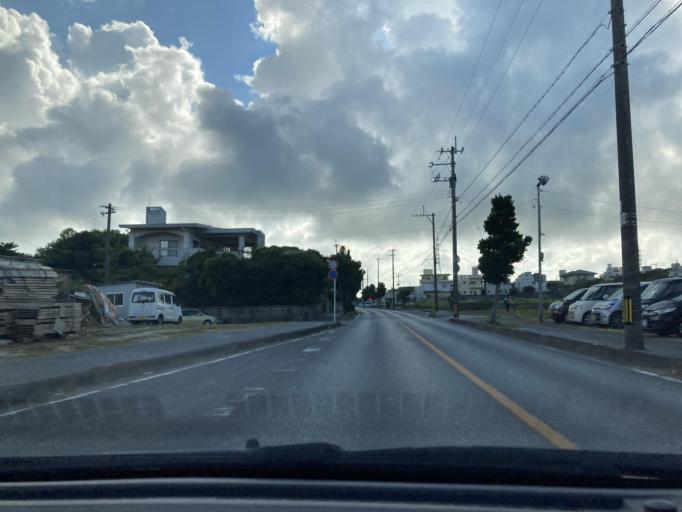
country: JP
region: Okinawa
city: Tomigusuku
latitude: 26.1747
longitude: 127.7222
